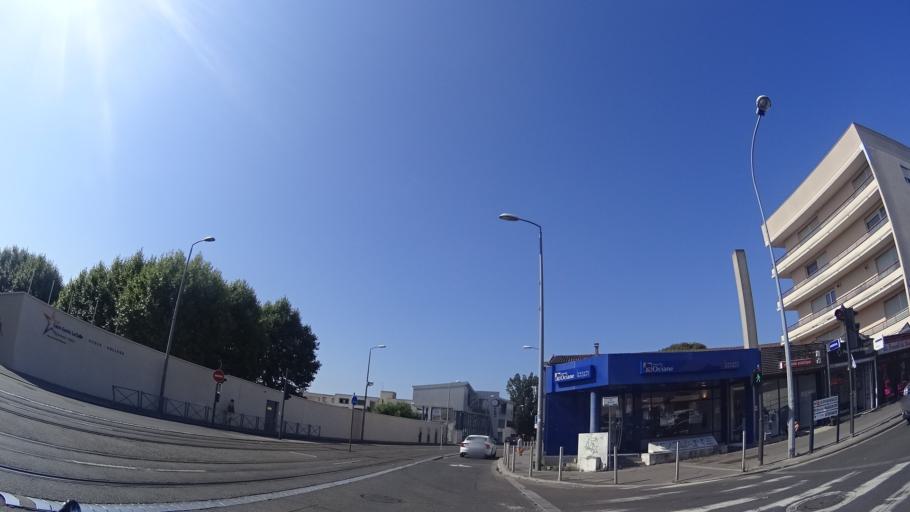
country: FR
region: Aquitaine
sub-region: Departement de la Gironde
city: Talence
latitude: 44.8166
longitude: -0.5859
